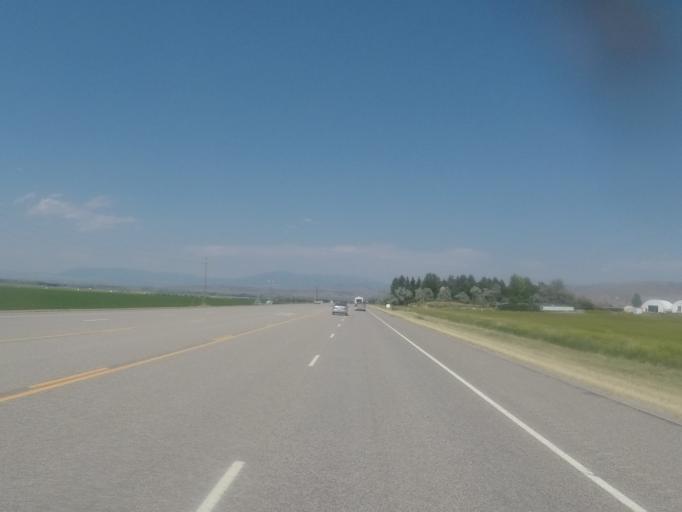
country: US
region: Montana
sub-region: Broadwater County
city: Townsend
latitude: 46.1389
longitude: -111.4790
